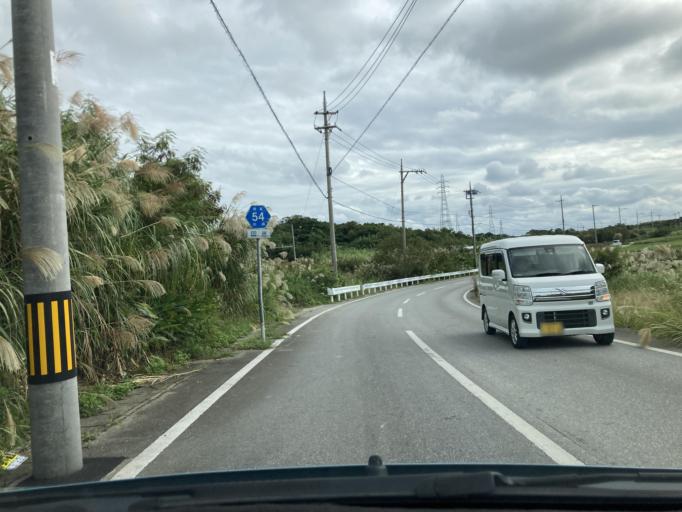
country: JP
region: Okinawa
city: Itoman
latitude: 26.1188
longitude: 127.6875
